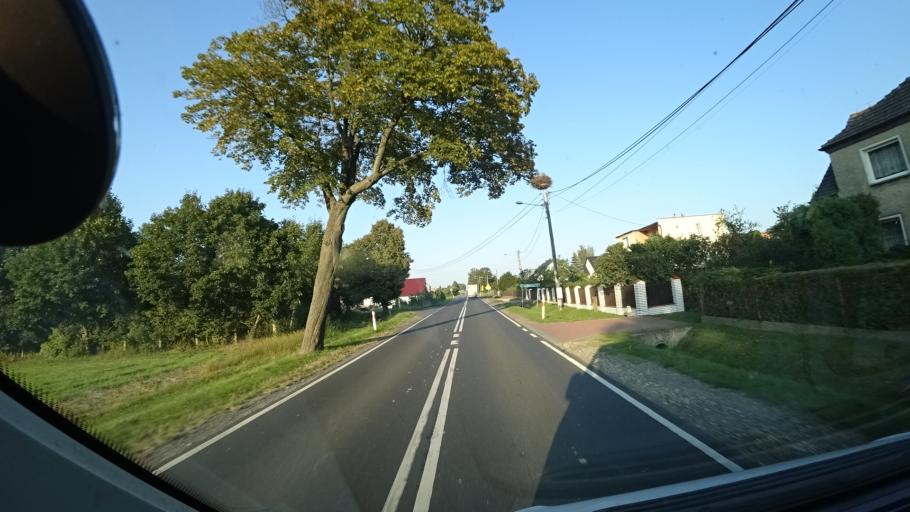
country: PL
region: Silesian Voivodeship
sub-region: Powiat gliwicki
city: Sosnicowice
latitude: 50.2729
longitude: 18.4541
